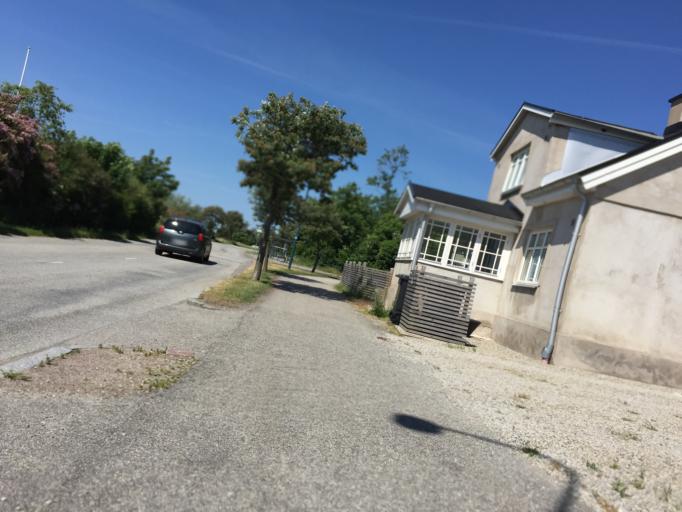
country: SE
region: Skane
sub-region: Trelleborgs Kommun
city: Trelleborg
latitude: 55.3582
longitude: 13.2315
